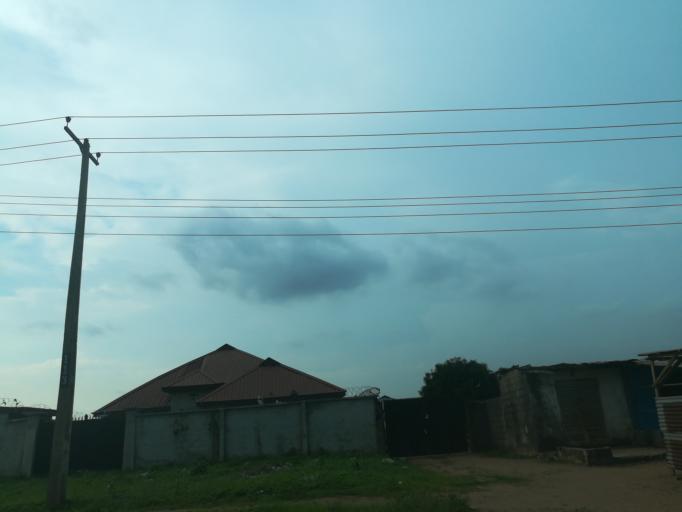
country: NG
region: Lagos
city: Ikorodu
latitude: 6.6124
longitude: 3.5983
